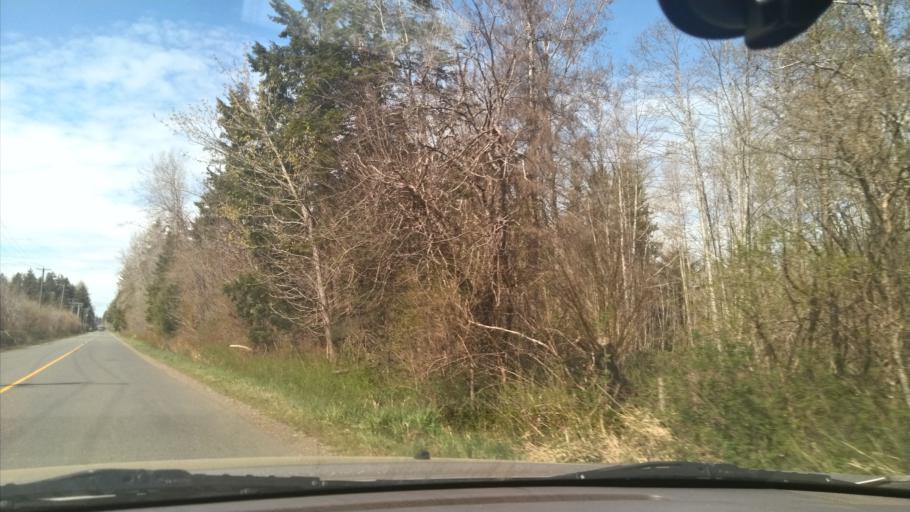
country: CA
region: British Columbia
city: Courtenay
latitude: 49.6983
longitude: -125.0149
